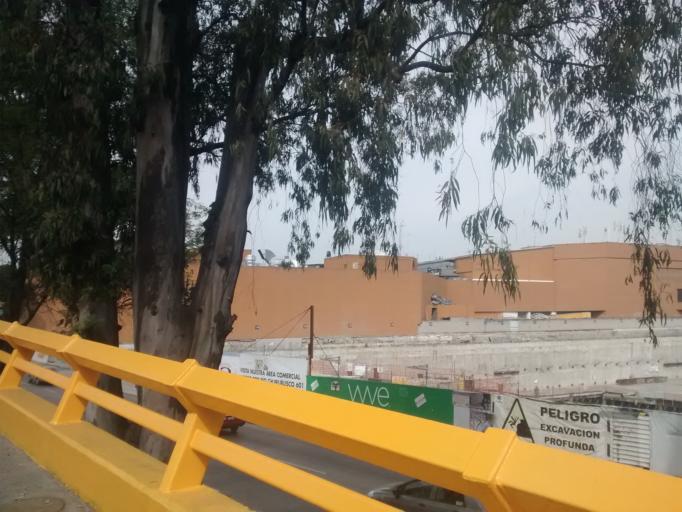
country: MX
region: Mexico City
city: Coyoacan
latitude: 19.3587
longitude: -99.1688
